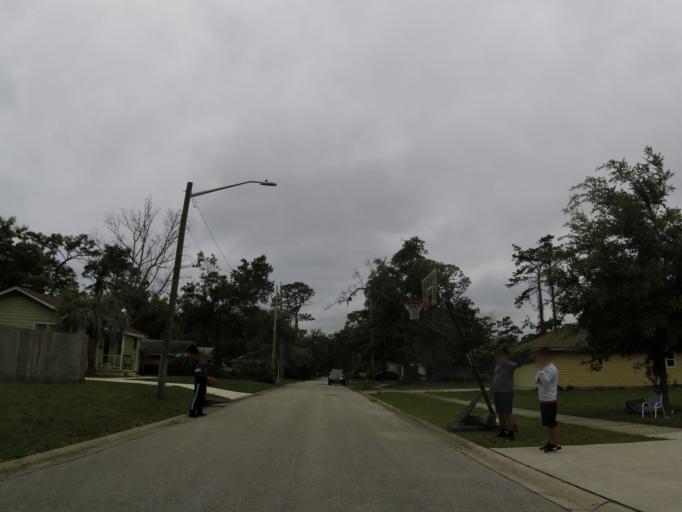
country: US
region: Florida
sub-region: Duval County
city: Jacksonville
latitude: 30.2927
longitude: -81.6412
